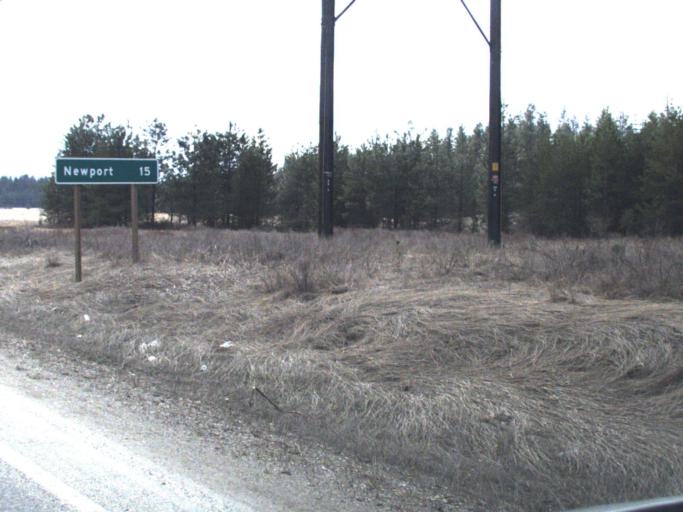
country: US
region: Washington
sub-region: Pend Oreille County
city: Newport
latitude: 48.3017
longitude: -117.2816
